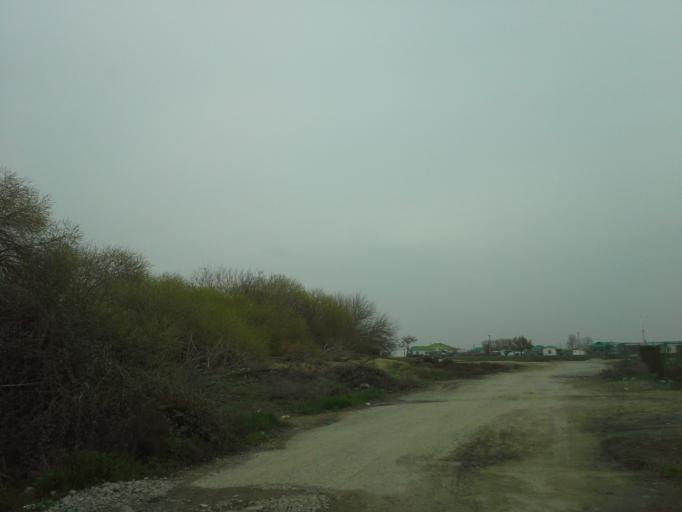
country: TM
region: Ahal
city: Abadan
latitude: 37.9690
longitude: 58.2219
